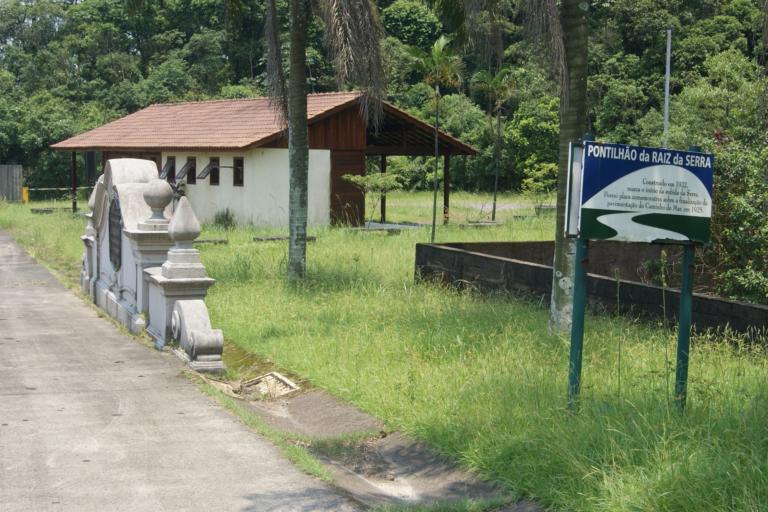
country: BR
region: Sao Paulo
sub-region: Cubatao
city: Cubatao
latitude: -23.8642
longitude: -46.4343
